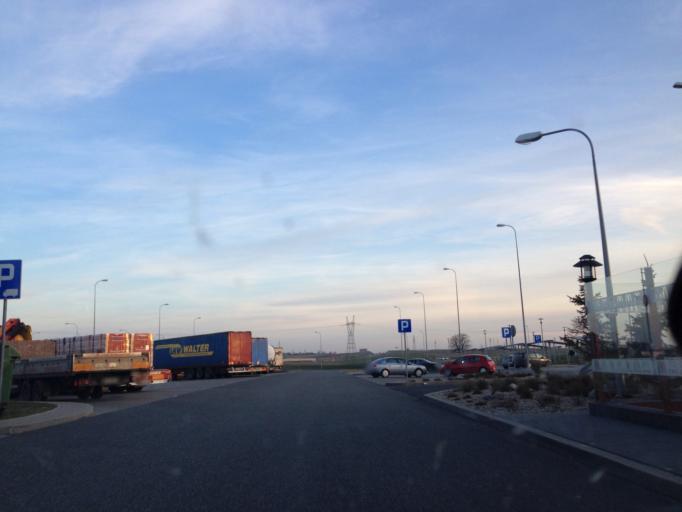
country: PL
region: Kujawsko-Pomorskie
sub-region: Powiat chelminski
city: Lisewo
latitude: 53.3415
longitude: 18.7081
